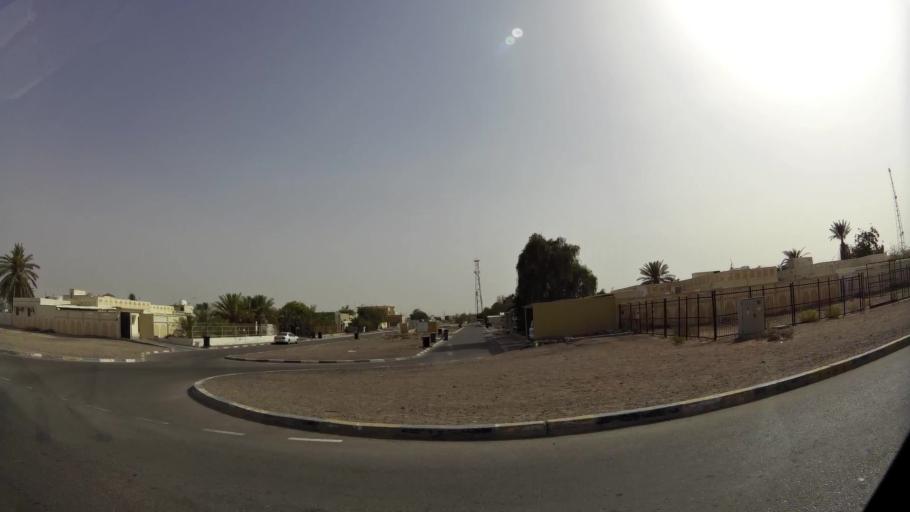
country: AE
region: Abu Dhabi
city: Al Ain
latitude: 24.2102
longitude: 55.5820
